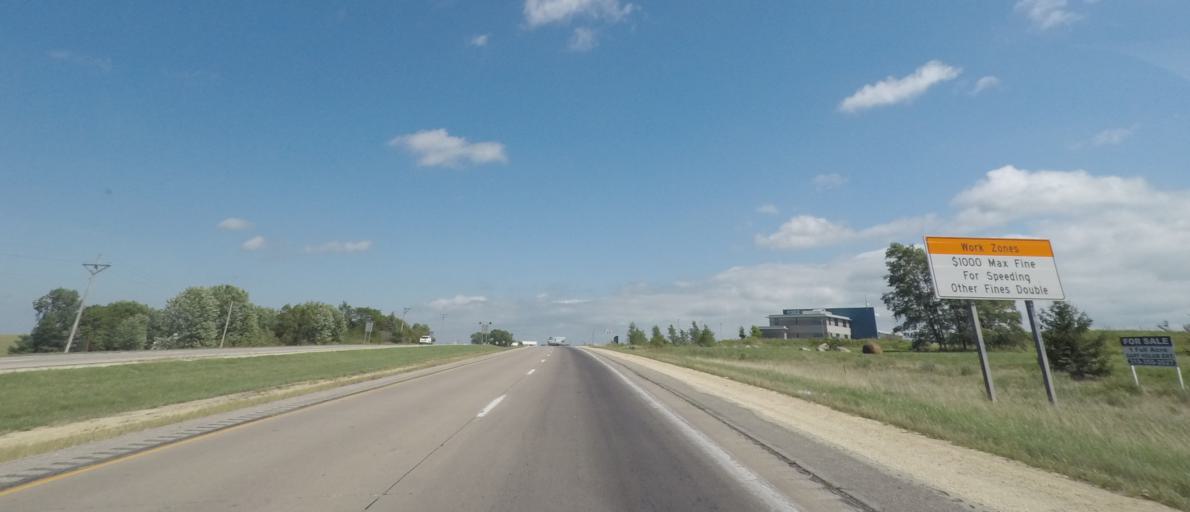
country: US
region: Iowa
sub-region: Linn County
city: Marion
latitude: 42.0355
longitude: -91.5439
